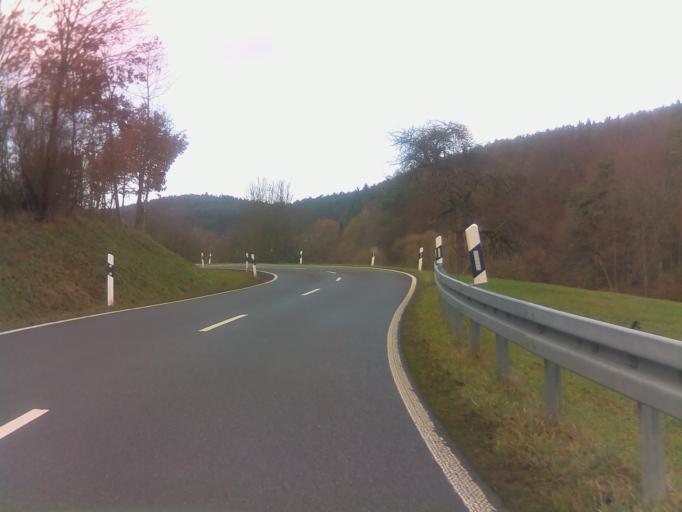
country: DE
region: Bavaria
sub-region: Regierungsbezirk Unterfranken
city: Stadtprozelten
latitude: 49.7998
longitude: 9.4187
